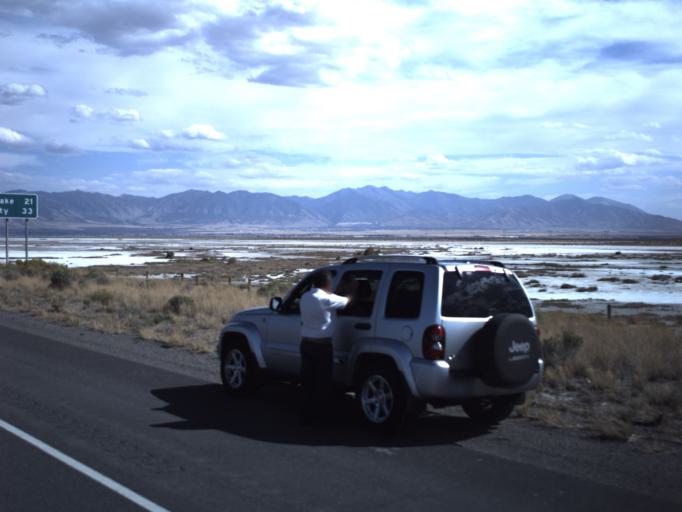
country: US
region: Utah
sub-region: Tooele County
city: Grantsville
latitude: 40.6824
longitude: -112.4329
